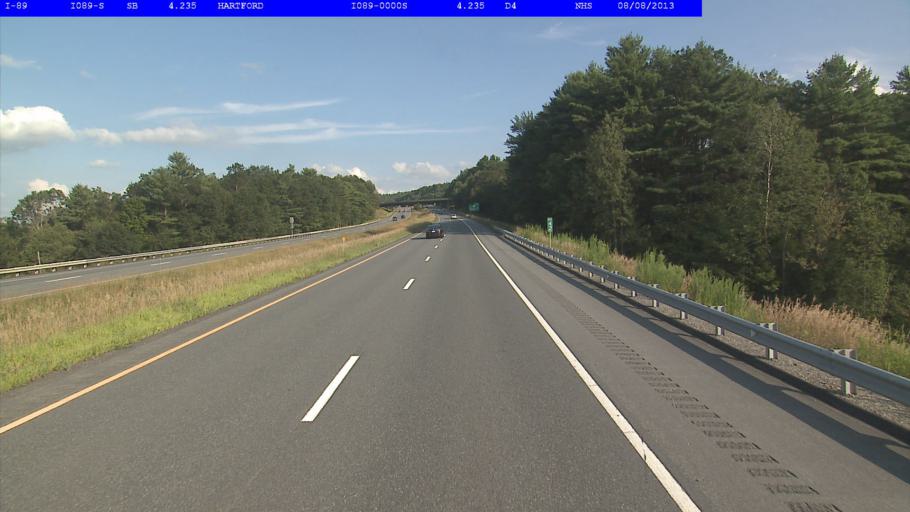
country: US
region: Vermont
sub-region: Windsor County
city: White River Junction
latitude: 43.6700
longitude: -72.3898
